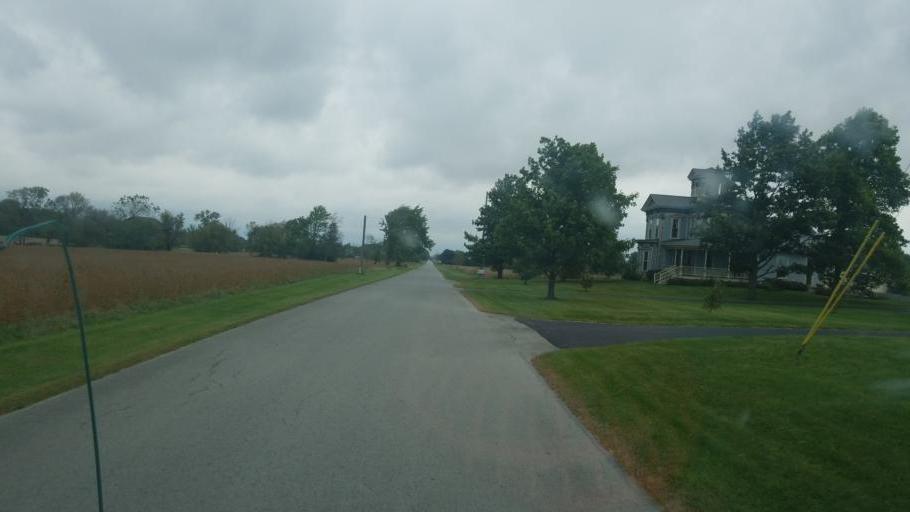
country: US
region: Ohio
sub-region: Seneca County
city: Fostoria
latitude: 41.0960
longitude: -83.5165
